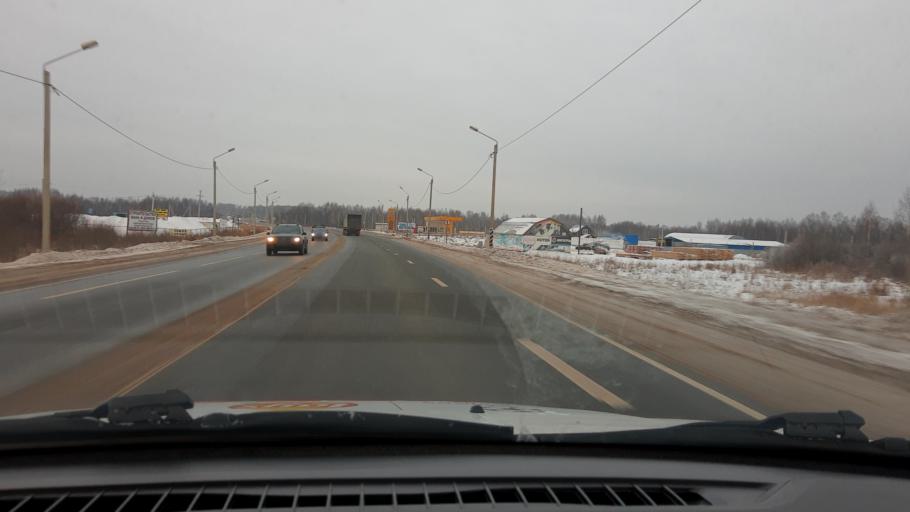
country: RU
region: Nizjnij Novgorod
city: Sitniki
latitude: 56.4989
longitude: 44.0253
